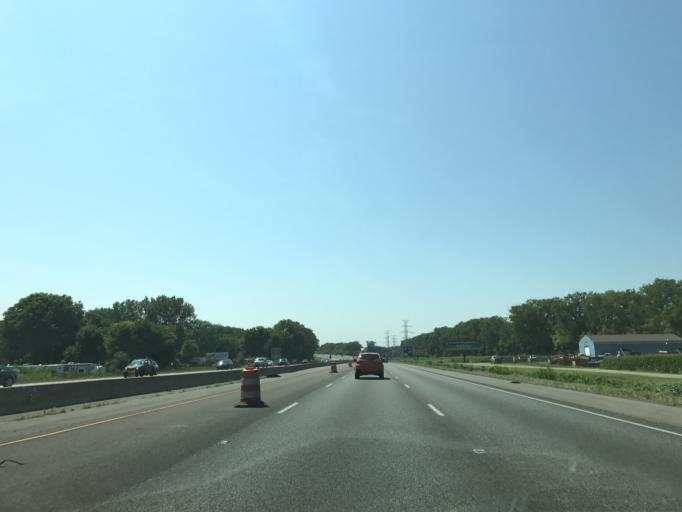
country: US
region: Indiana
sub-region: Porter County
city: Ogden Dunes
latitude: 41.5982
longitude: -87.2050
